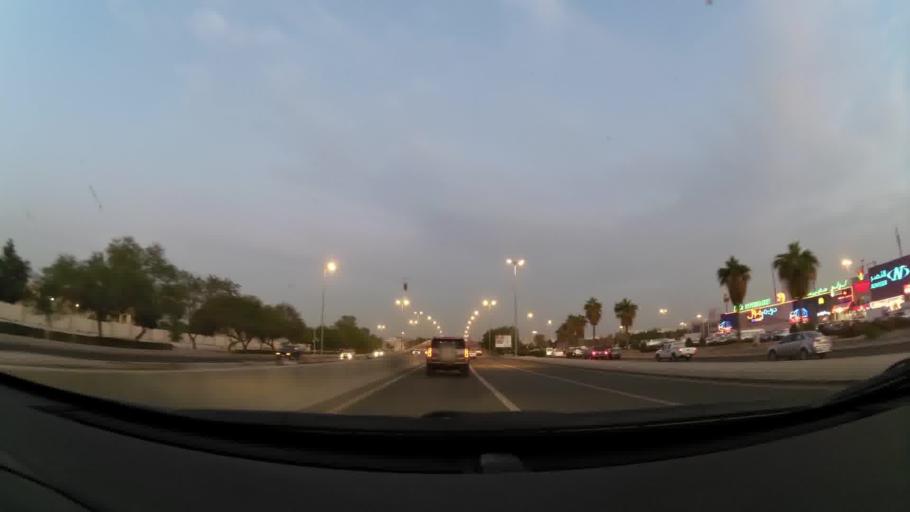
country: KW
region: Al Asimah
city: Ash Shamiyah
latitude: 29.3166
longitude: 47.9575
